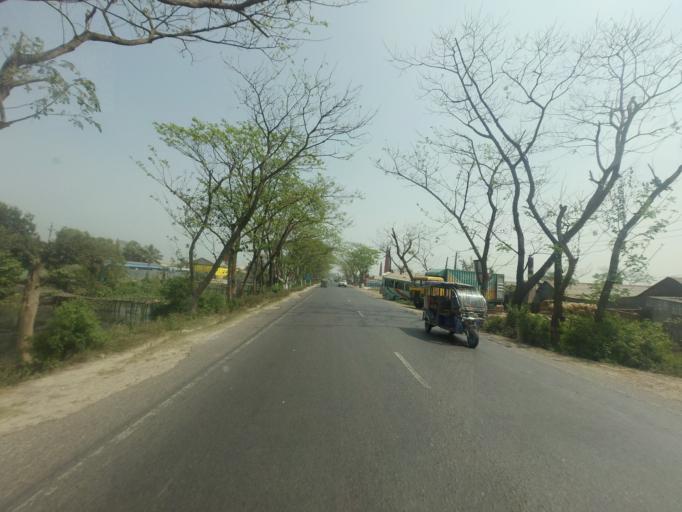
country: BD
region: Dhaka
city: Bhairab Bazar
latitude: 24.0445
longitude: 91.0653
